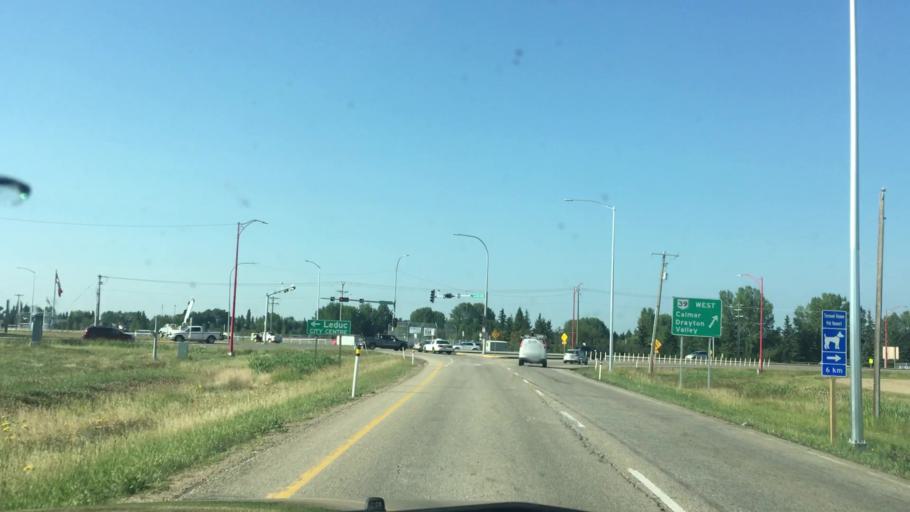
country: CA
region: Alberta
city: Leduc
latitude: 53.2657
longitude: -113.5648
